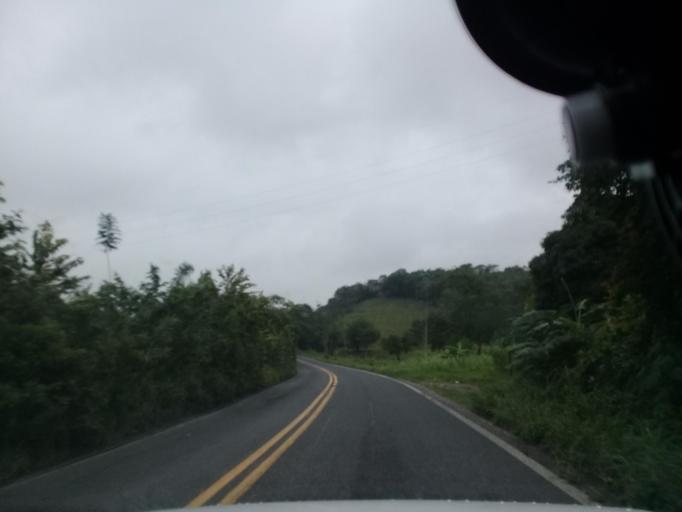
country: MX
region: Veracruz
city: Platon Sanchez
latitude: 21.2416
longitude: -98.3650
